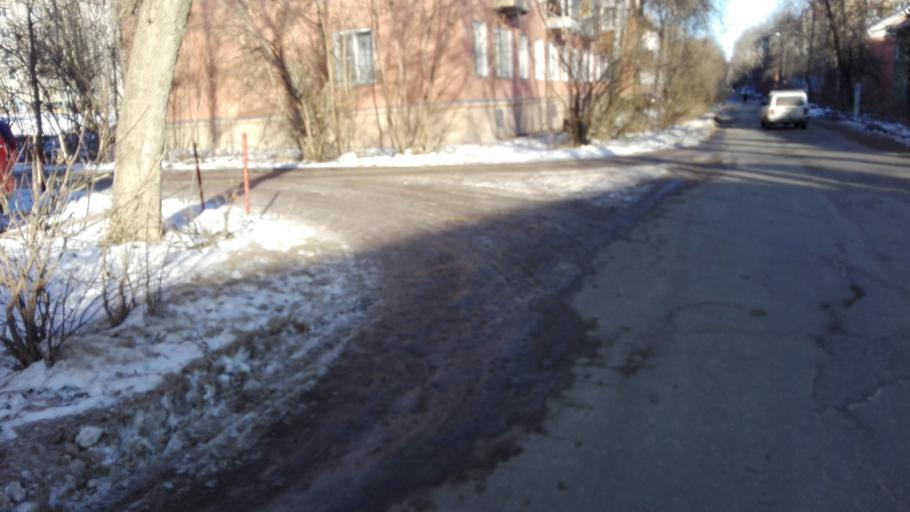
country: RU
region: Tula
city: Kosaya Gora
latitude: 54.1178
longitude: 37.5398
